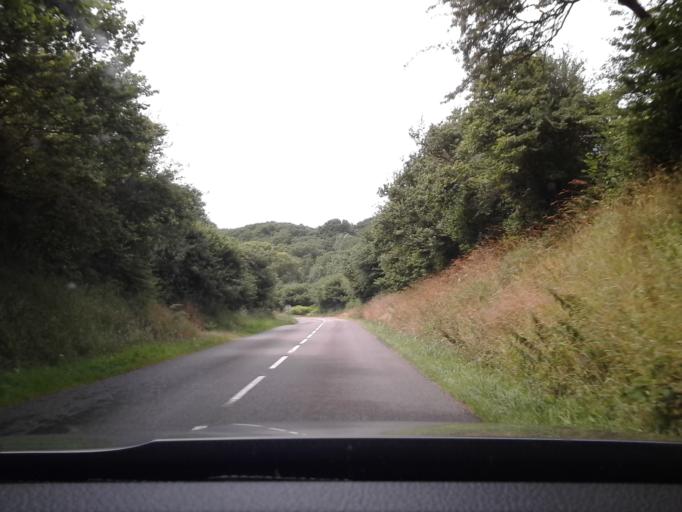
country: FR
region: Lower Normandy
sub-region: Departement de la Manche
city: Beaumont-Hague
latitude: 49.6713
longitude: -1.8237
